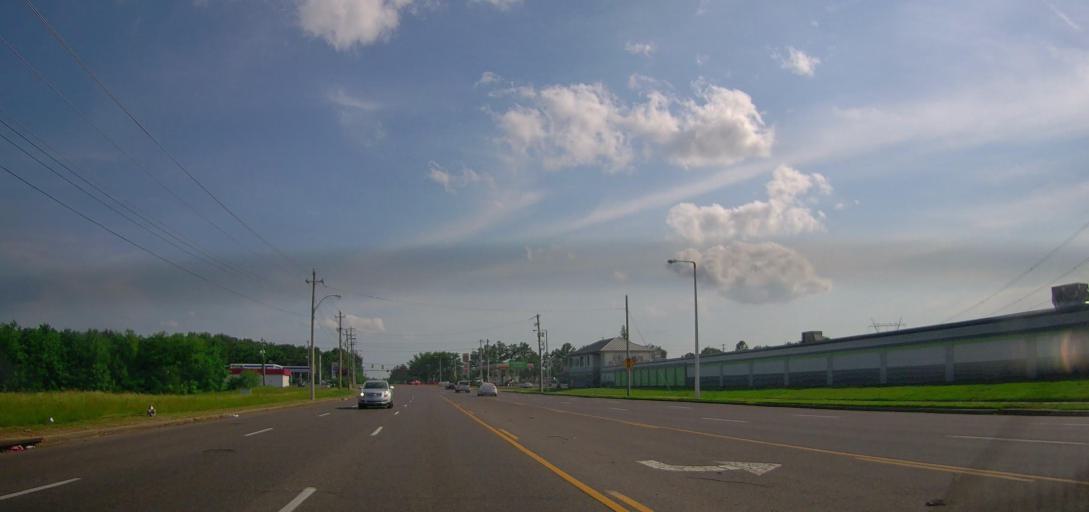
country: US
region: Mississippi
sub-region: De Soto County
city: Olive Branch
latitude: 35.0225
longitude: -89.8486
